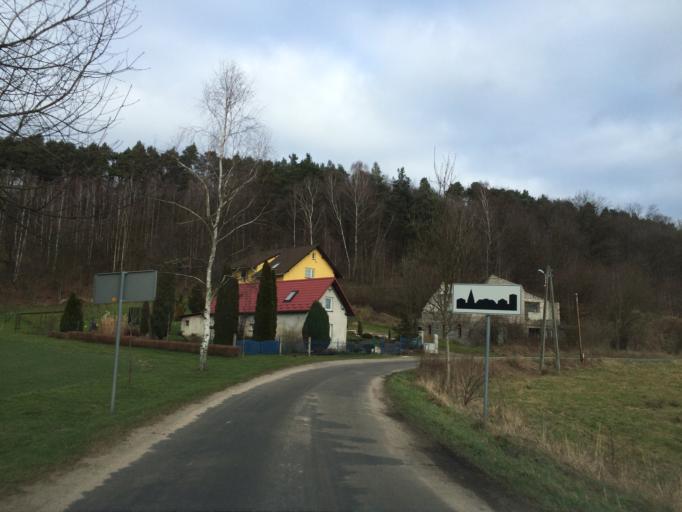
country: PL
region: Lower Silesian Voivodeship
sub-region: Powiat lwowecki
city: Lwowek Slaski
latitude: 51.1579
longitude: 15.5779
